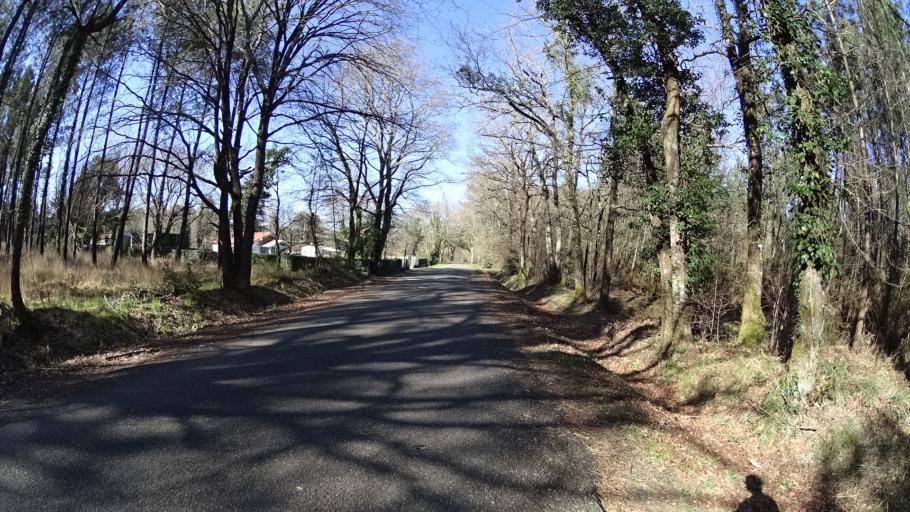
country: FR
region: Aquitaine
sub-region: Departement des Landes
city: Mees
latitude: 43.7415
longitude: -1.0969
